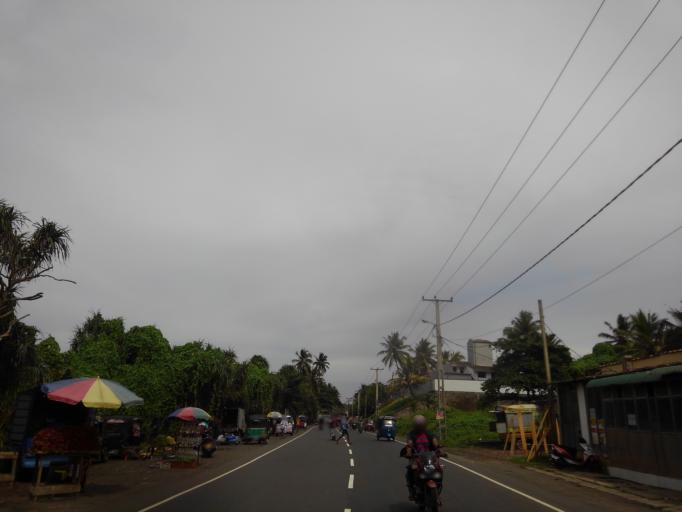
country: LK
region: Western
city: Beruwala
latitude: 6.4794
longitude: 79.9833
